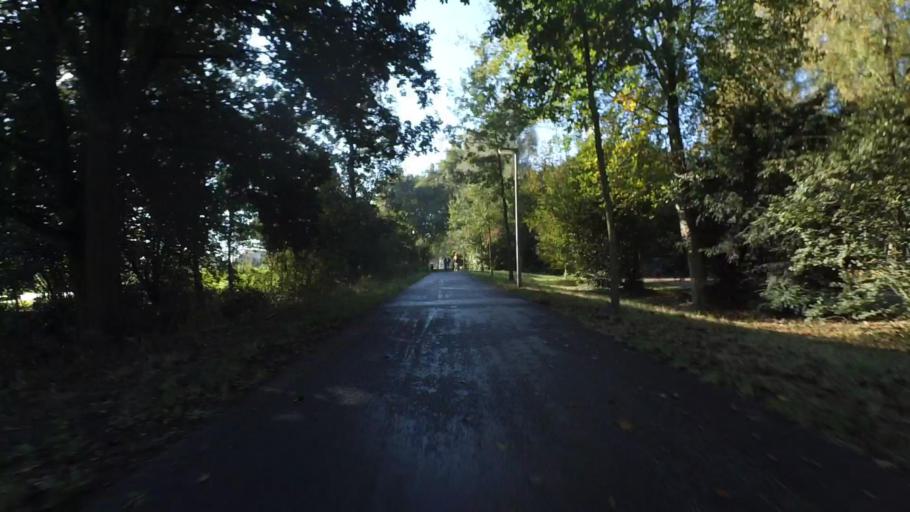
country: NL
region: Gelderland
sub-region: Gemeente Epe
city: Vaassen
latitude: 52.2923
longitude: 5.9754
